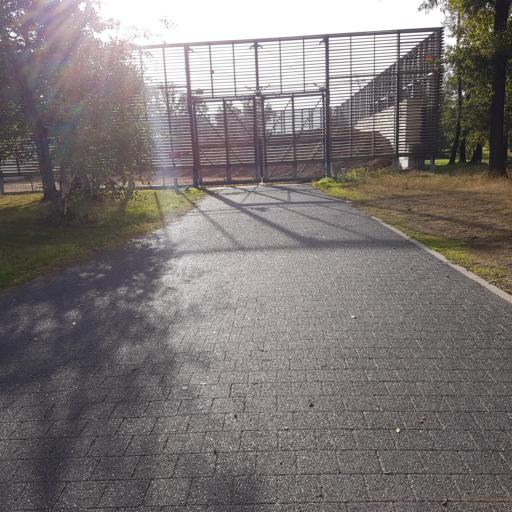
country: NL
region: North Brabant
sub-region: Gemeente Eindhoven
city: Meerhoven
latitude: 51.4431
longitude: 5.3972
